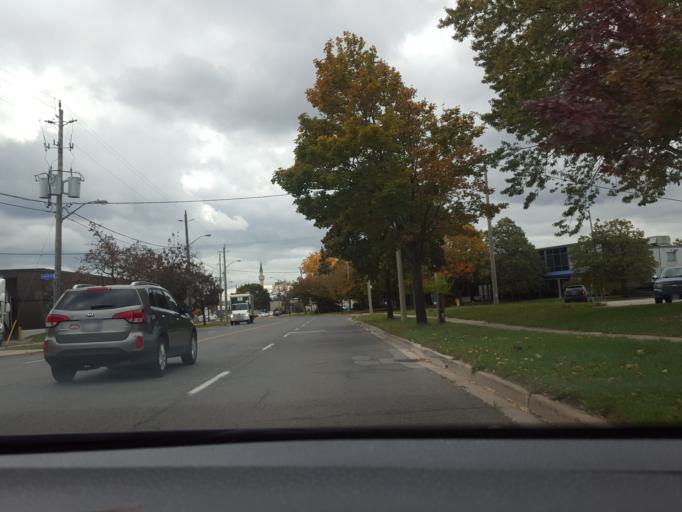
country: CA
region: Ontario
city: Etobicoke
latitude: 43.6230
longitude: -79.5499
